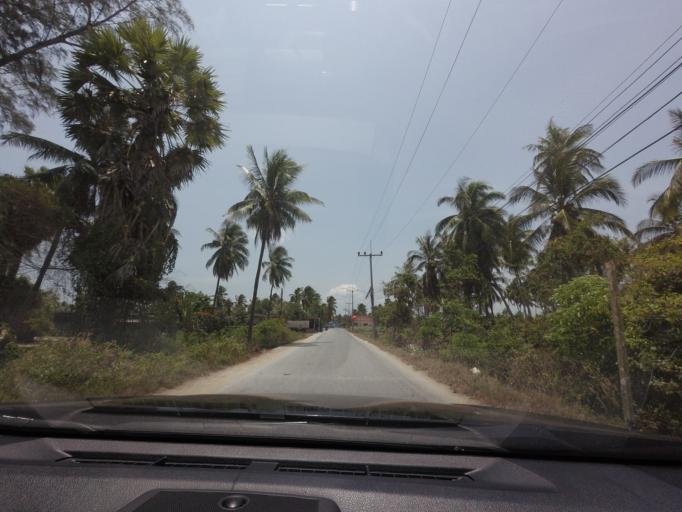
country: TH
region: Pattani
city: Yaring
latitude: 6.8976
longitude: 101.3737
